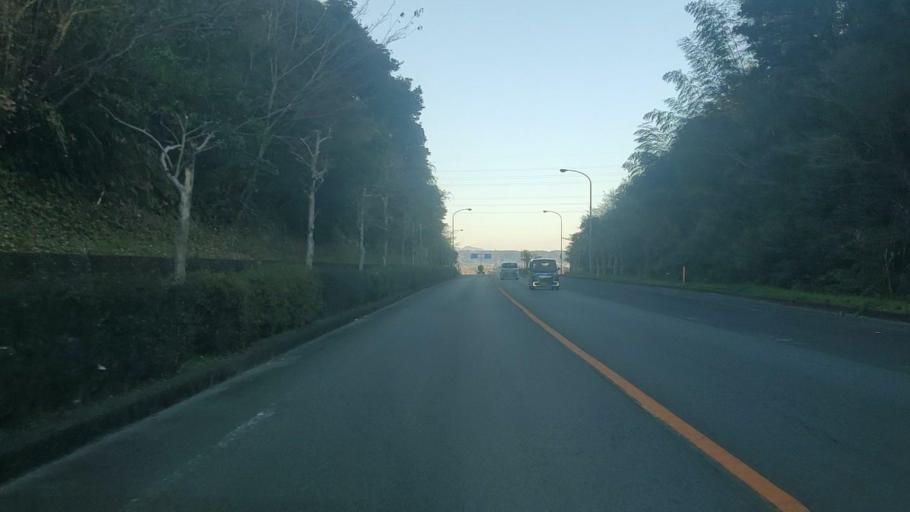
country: JP
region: Miyazaki
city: Tsuma
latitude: 32.0307
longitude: 131.4645
